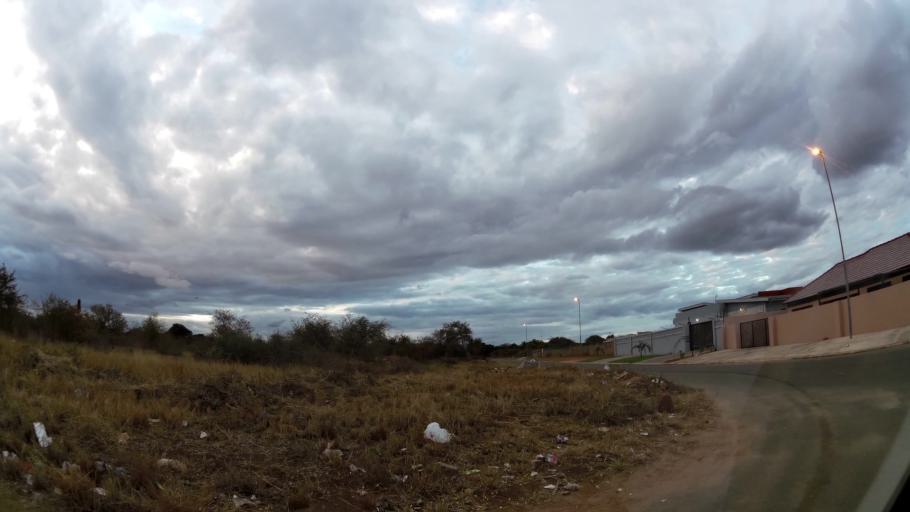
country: ZA
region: Limpopo
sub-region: Waterberg District Municipality
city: Mokopane
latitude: -24.1938
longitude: 28.9990
